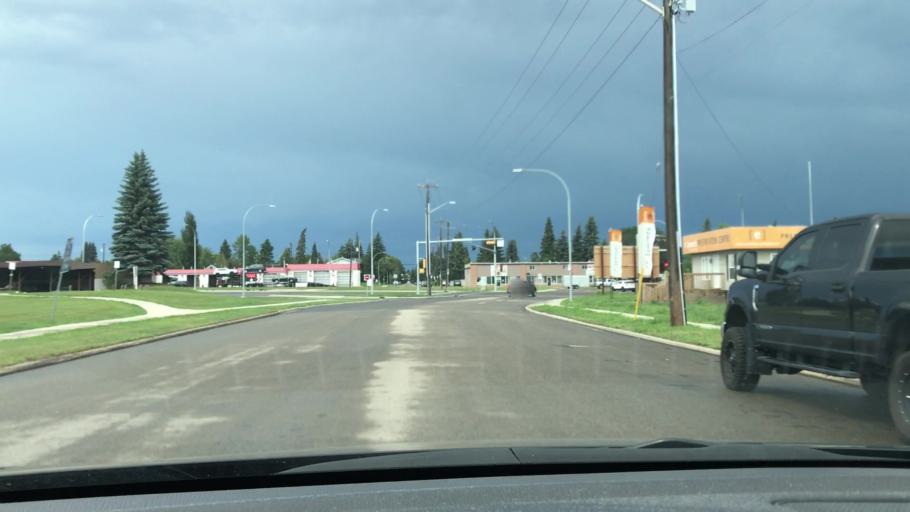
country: CA
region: Alberta
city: Edmonton
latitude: 53.5165
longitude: -113.4369
